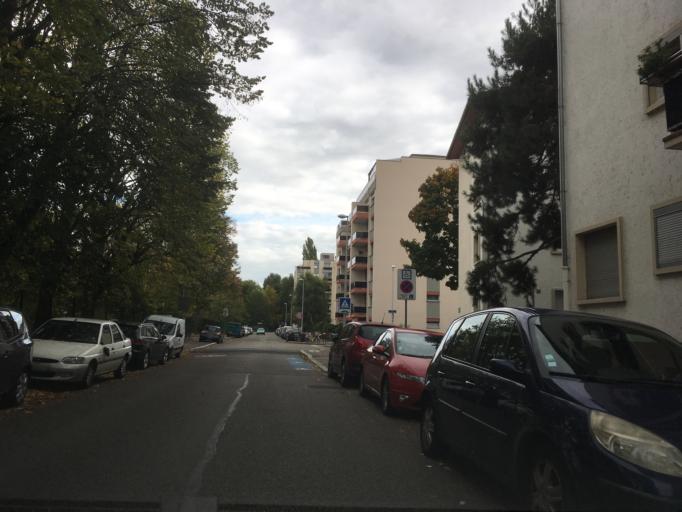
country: FR
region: Alsace
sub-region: Departement du Bas-Rhin
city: Strasbourg
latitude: 48.5625
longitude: 7.7690
